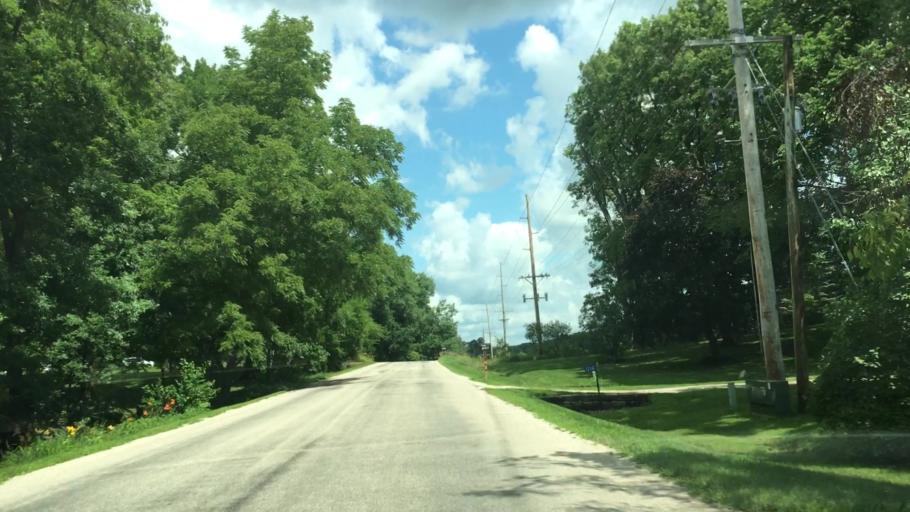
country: US
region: Iowa
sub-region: Linn County
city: Lisbon
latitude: 41.8437
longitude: -91.3857
